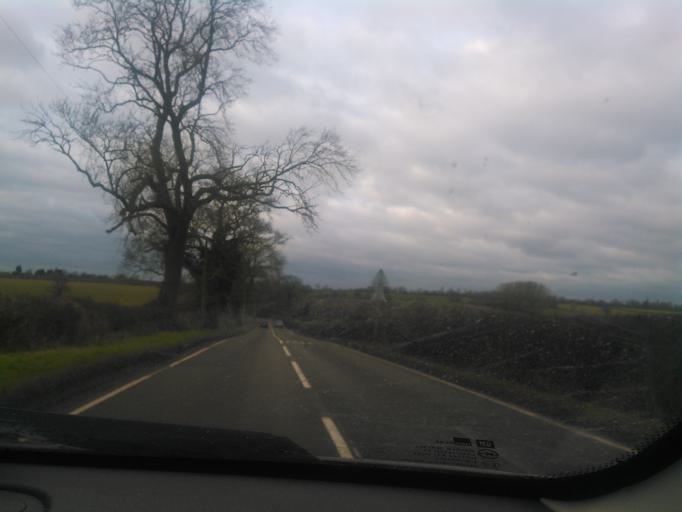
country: GB
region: England
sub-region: Leicestershire
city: Wigston Magna
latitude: 52.5659
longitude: -1.0681
